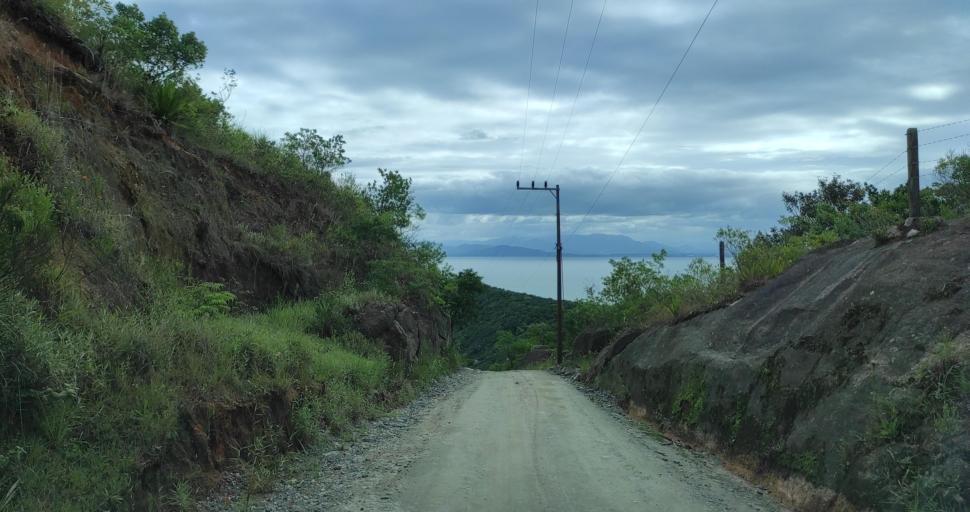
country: BR
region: Santa Catarina
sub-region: Porto Belo
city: Porto Belo
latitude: -27.2131
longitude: -48.5058
